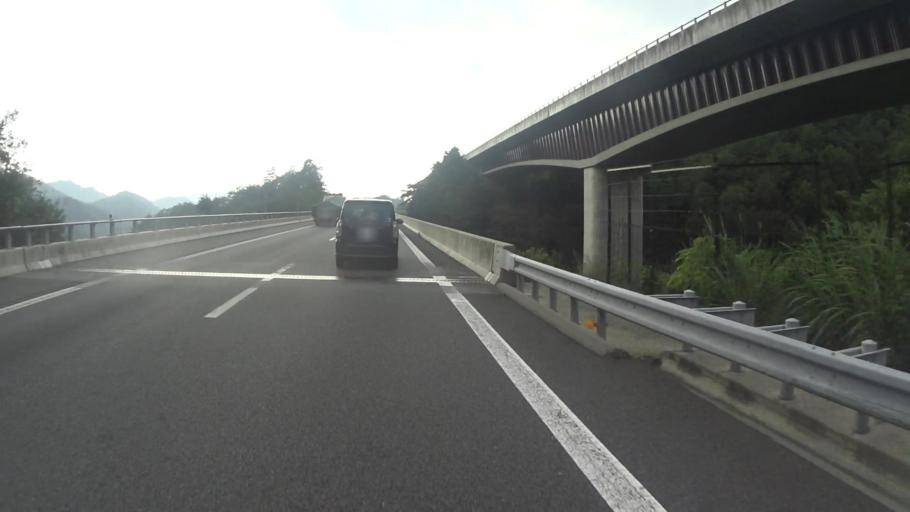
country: JP
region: Shiga Prefecture
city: Kusatsu
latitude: 34.9317
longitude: 136.0498
